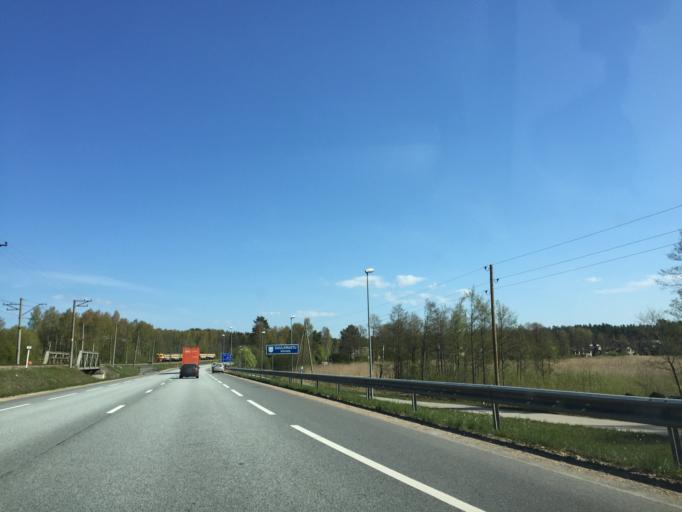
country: LV
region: Carnikava
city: Carnikava
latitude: 57.1864
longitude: 24.3455
